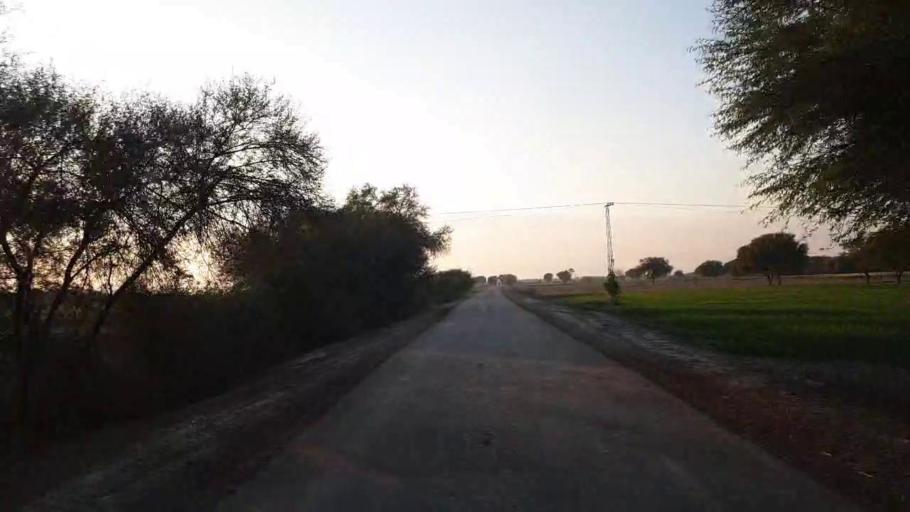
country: PK
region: Sindh
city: Shahpur Chakar
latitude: 26.1555
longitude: 68.5594
